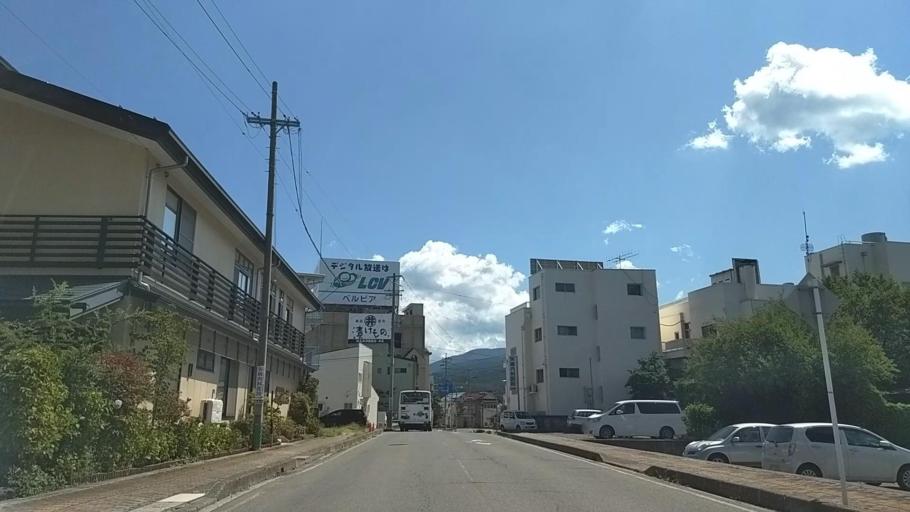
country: JP
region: Nagano
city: Chino
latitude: 35.9955
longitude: 138.1504
